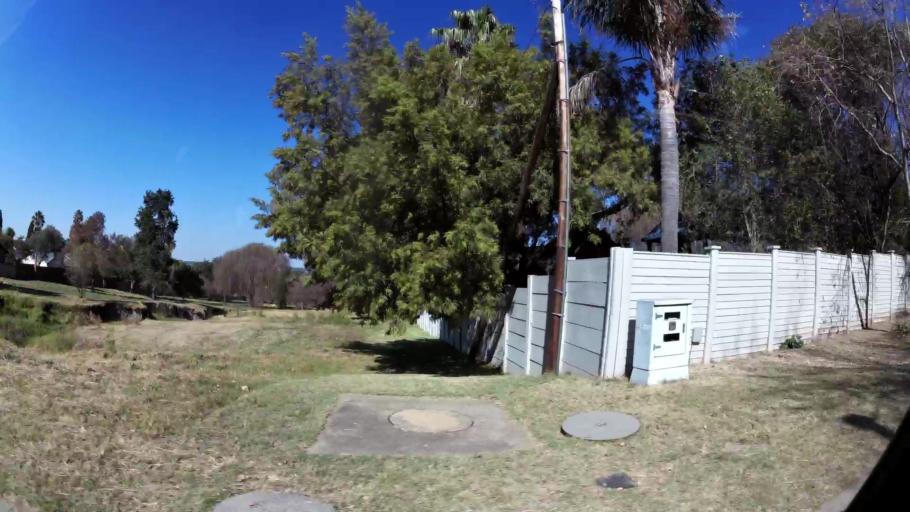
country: ZA
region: Gauteng
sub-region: City of Johannesburg Metropolitan Municipality
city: Roodepoort
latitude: -26.1013
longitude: 27.9512
